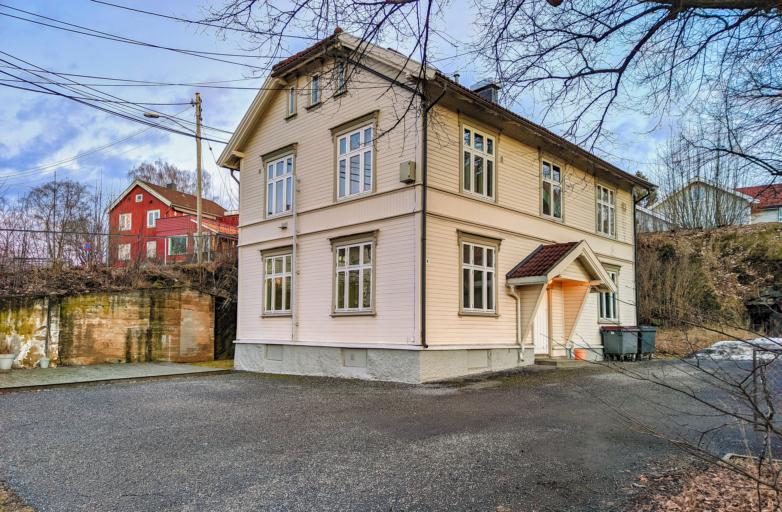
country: NO
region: Oslo
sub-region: Oslo
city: Oslo
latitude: 59.9187
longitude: 10.8173
